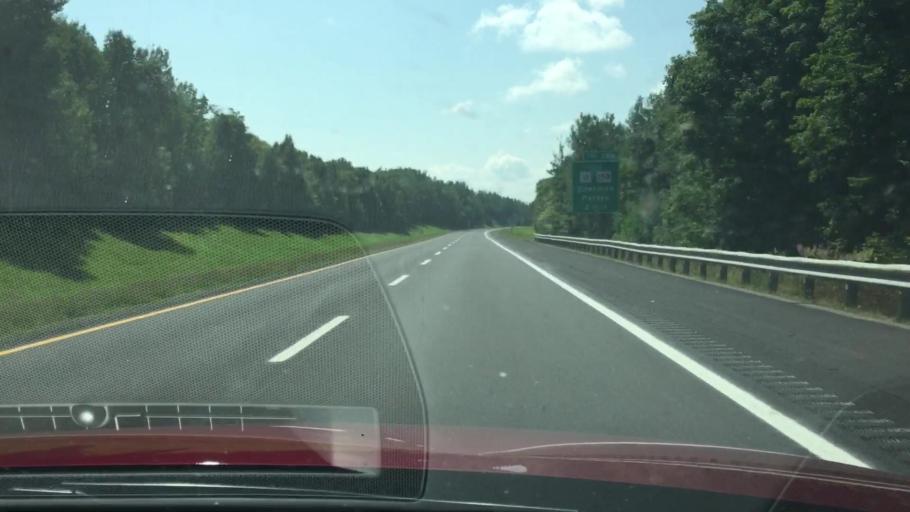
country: US
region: Maine
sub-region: Penobscot County
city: Patten
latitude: 45.9086
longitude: -68.3817
